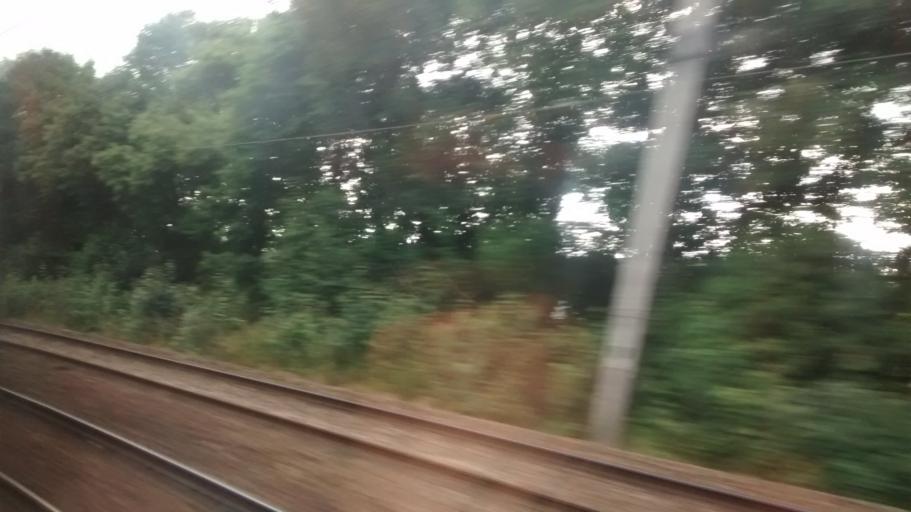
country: FR
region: Brittany
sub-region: Departement d'Ille-et-Vilaine
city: Vitre
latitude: 48.1206
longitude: -1.2228
